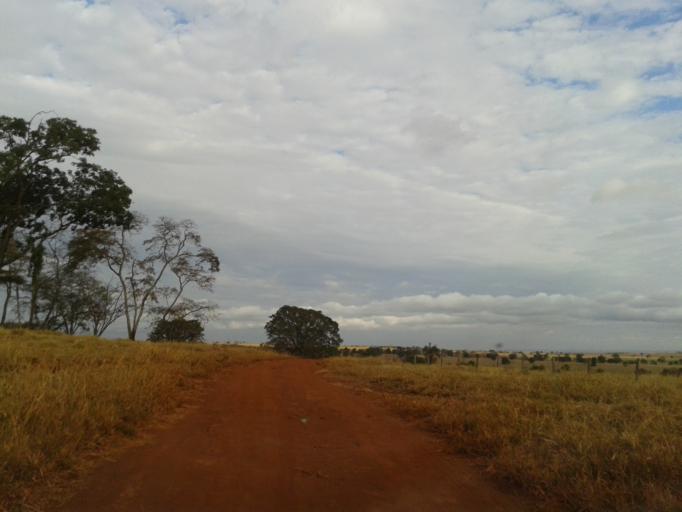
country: BR
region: Minas Gerais
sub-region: Santa Vitoria
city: Santa Vitoria
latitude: -18.7341
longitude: -50.2275
